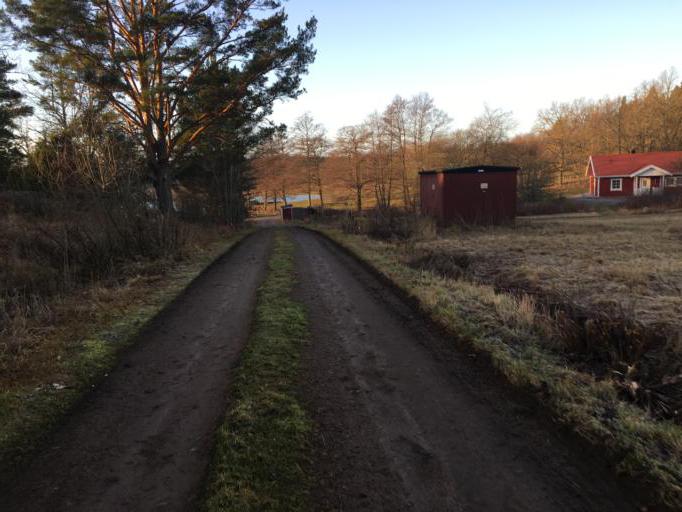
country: SE
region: Kalmar
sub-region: Vasterviks Kommun
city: Vaestervik
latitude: 57.6267
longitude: 16.5302
